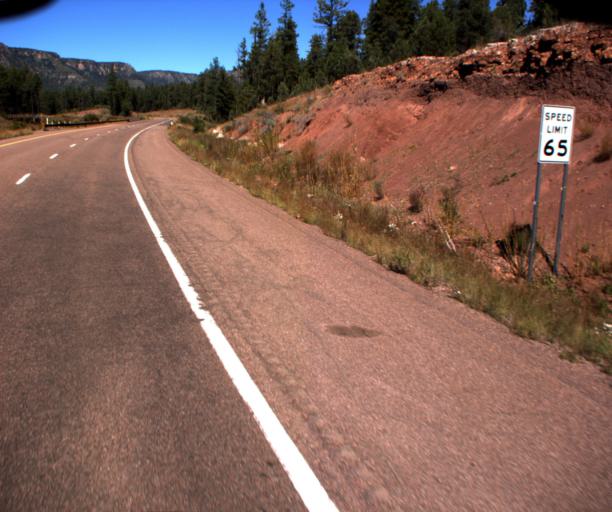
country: US
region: Arizona
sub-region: Gila County
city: Star Valley
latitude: 34.3076
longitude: -110.9963
